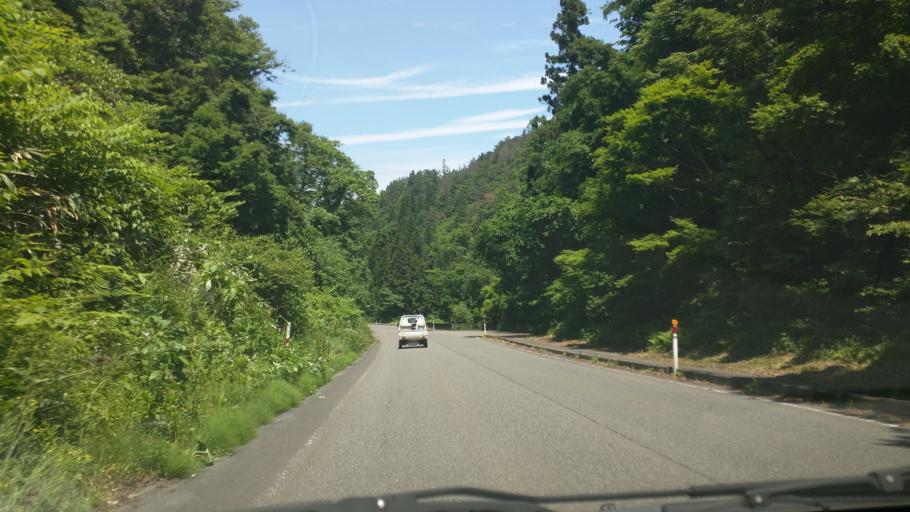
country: JP
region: Fukushima
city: Kitakata
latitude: 37.5192
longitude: 139.7221
